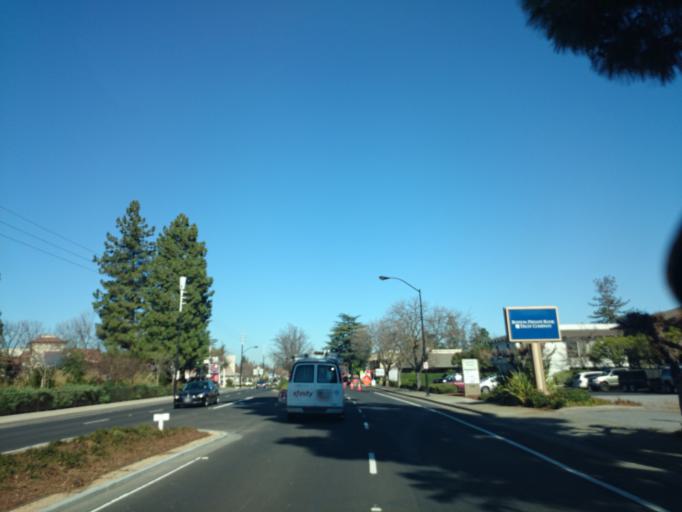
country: US
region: California
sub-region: Santa Clara County
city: Los Altos
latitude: 37.3761
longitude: -122.1142
